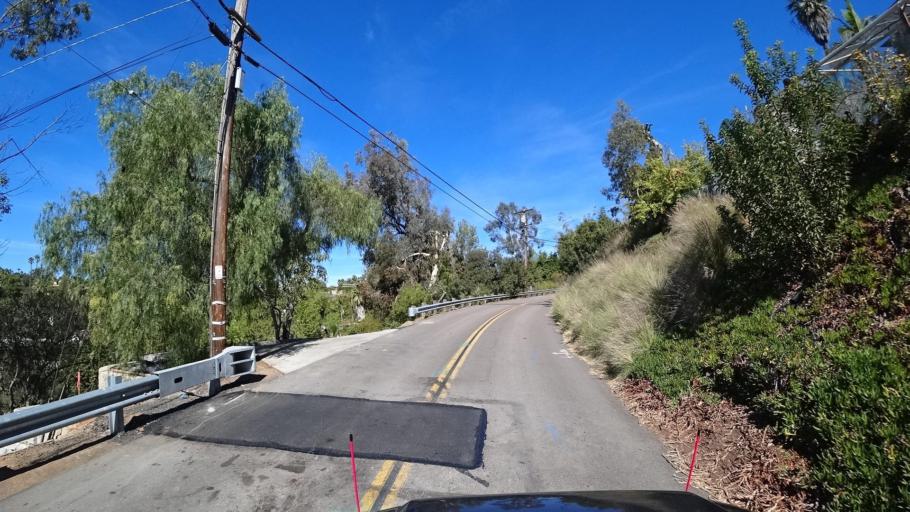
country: US
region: California
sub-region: San Diego County
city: Casa de Oro-Mount Helix
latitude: 32.7607
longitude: -116.9694
